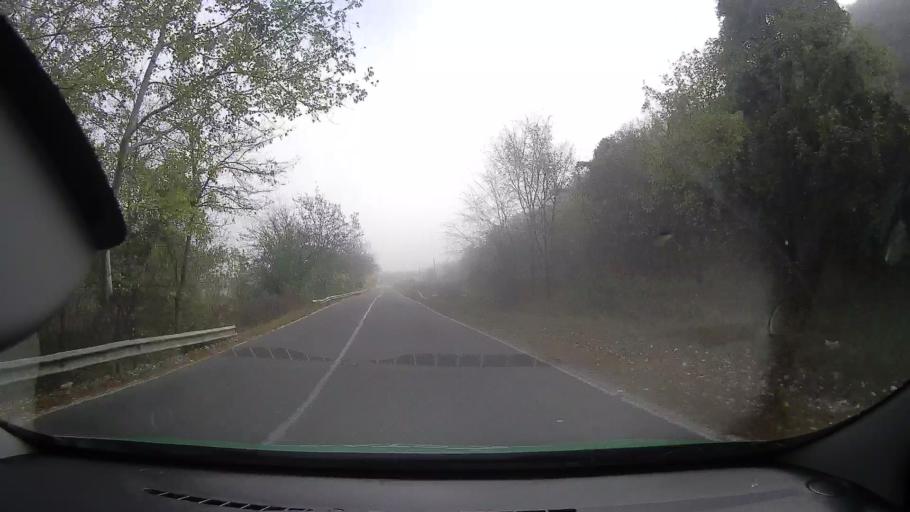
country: RO
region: Tulcea
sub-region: Comuna Nufaru
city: Nufaru
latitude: 45.1464
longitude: 28.9098
